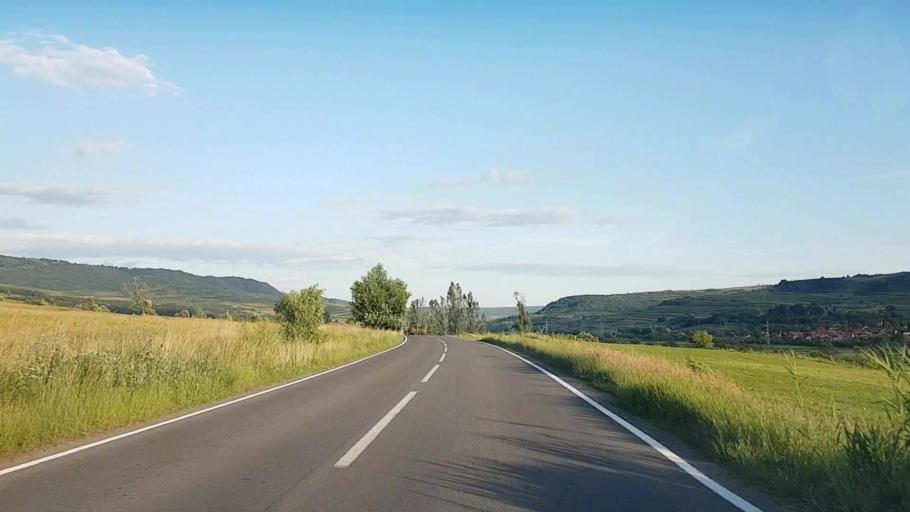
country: RO
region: Harghita
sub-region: Comuna Praid
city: Ocna de Jos
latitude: 46.5363
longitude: 25.1322
